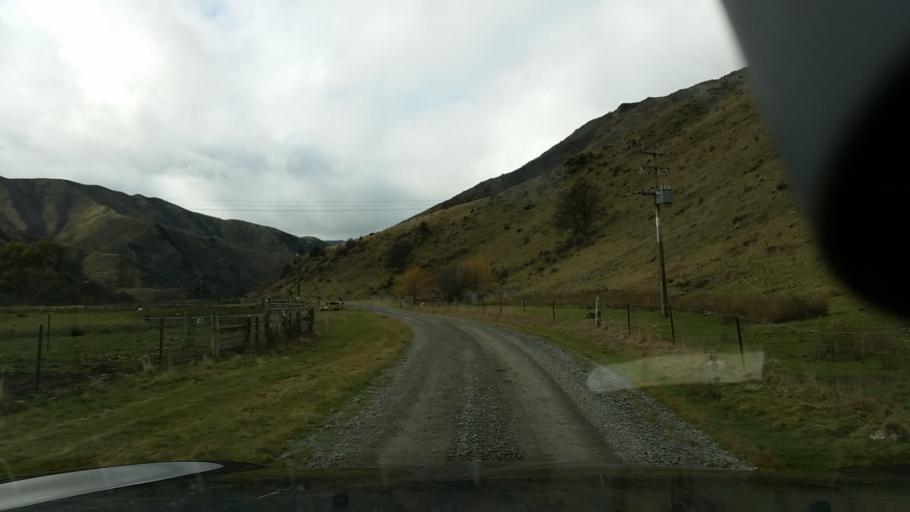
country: NZ
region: Tasman
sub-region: Tasman District
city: Brightwater
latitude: -41.7357
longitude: 173.4247
